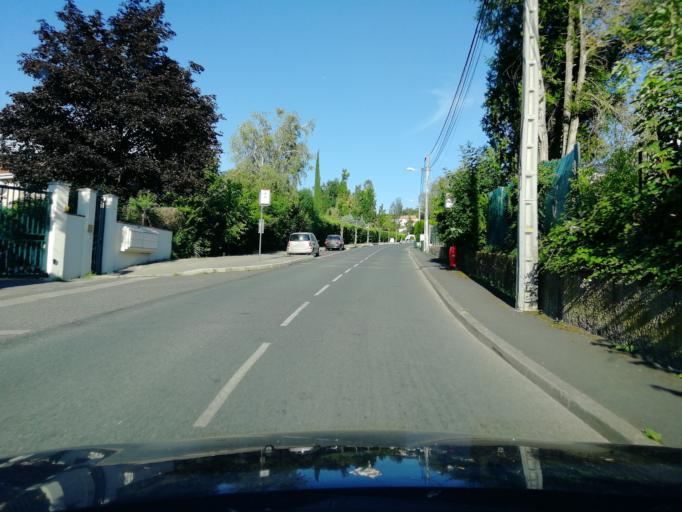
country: FR
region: Rhone-Alpes
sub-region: Departement du Rhone
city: Fontaines-Saint-Martin
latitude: 45.8462
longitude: 4.8611
